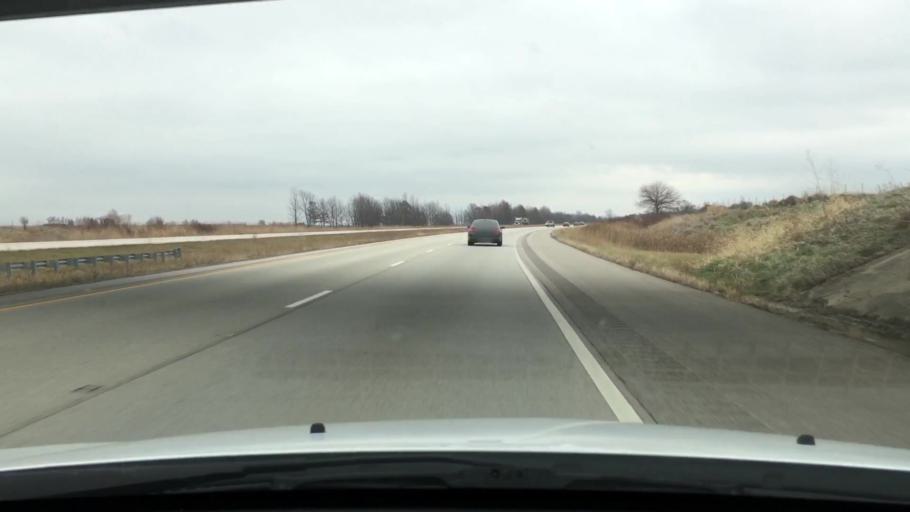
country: US
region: Illinois
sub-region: Sangamon County
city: New Berlin
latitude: 39.7513
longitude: -89.8000
